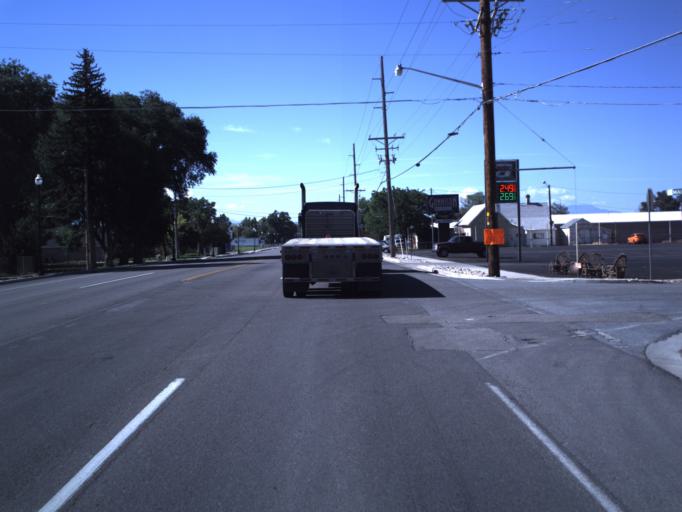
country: US
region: Utah
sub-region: Sanpete County
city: Gunnison
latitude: 39.1459
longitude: -111.8189
